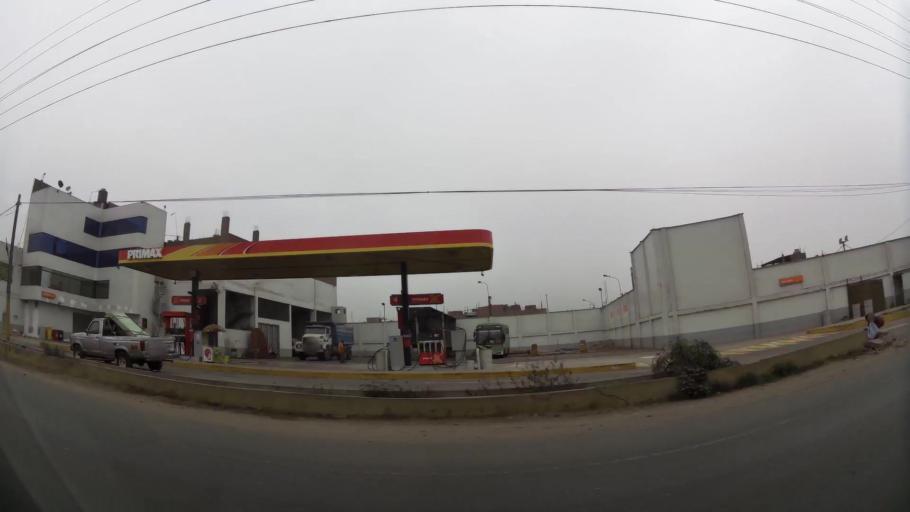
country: PE
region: Lima
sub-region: Lima
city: Santa Maria
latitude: -12.0122
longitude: -76.8781
